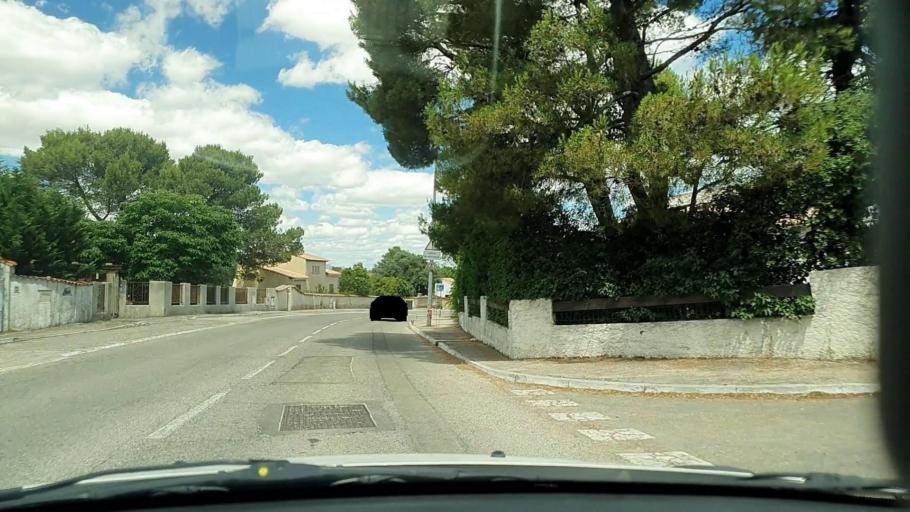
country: FR
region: Languedoc-Roussillon
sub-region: Departement du Gard
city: Poulx
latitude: 43.9065
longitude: 4.4213
